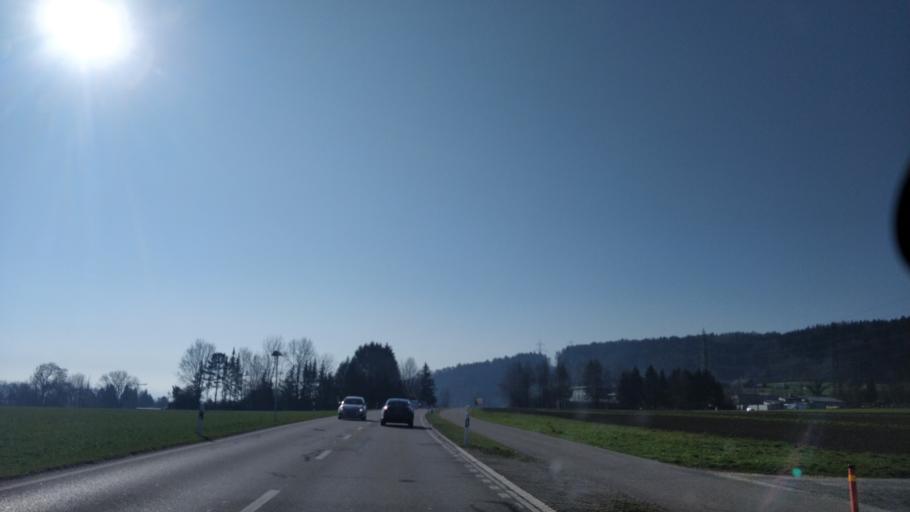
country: CH
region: Zurich
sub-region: Bezirk Uster
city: Dubendorf
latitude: 47.3832
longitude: 8.6226
